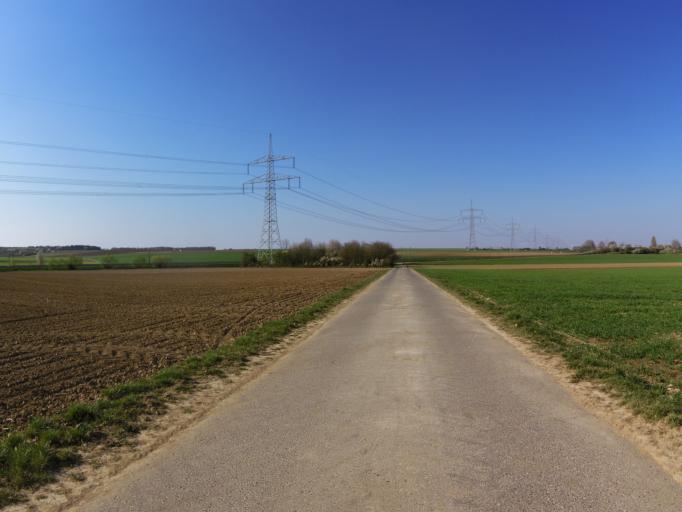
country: DE
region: Bavaria
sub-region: Regierungsbezirk Unterfranken
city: Oberpleichfeld
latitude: 49.8298
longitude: 10.0905
